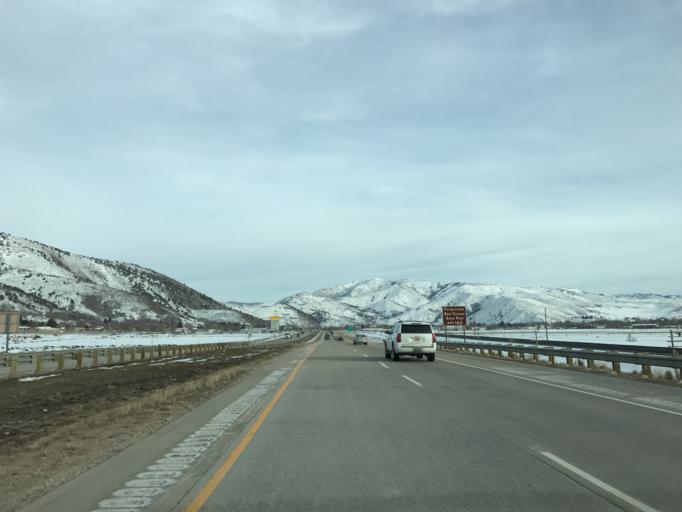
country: US
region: Utah
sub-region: Morgan County
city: Morgan
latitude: 41.0544
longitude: -111.6913
